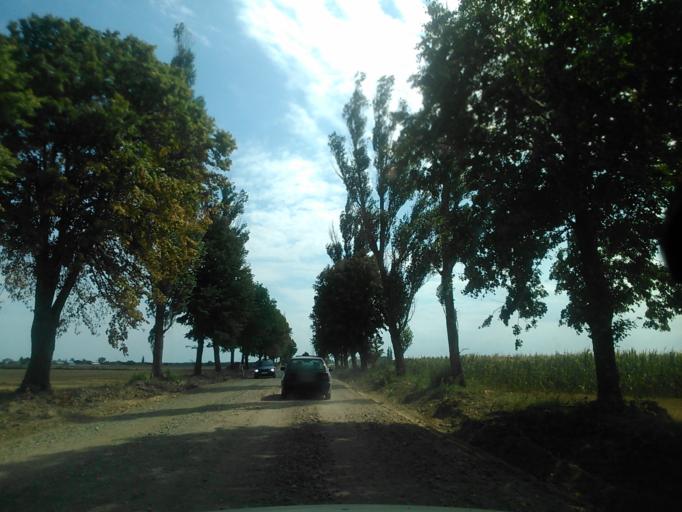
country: PL
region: Warmian-Masurian Voivodeship
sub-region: Powiat dzialdowski
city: Ilowo -Osada
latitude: 53.1837
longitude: 20.2885
